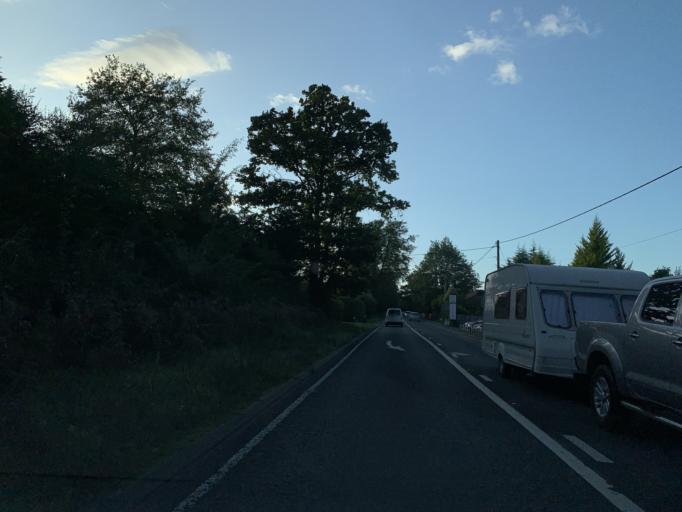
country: GB
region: England
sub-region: Hampshire
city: West Wellow
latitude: 50.9640
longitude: -1.5697
